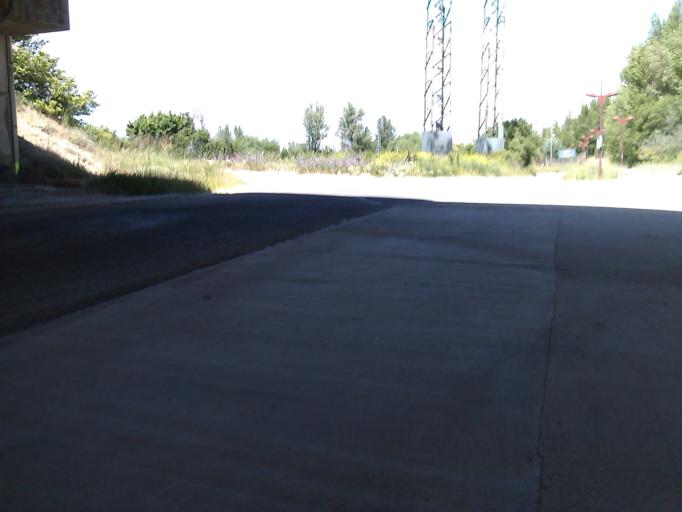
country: ES
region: Castille and Leon
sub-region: Provincia de Leon
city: Leon
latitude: 42.5862
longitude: -5.5519
